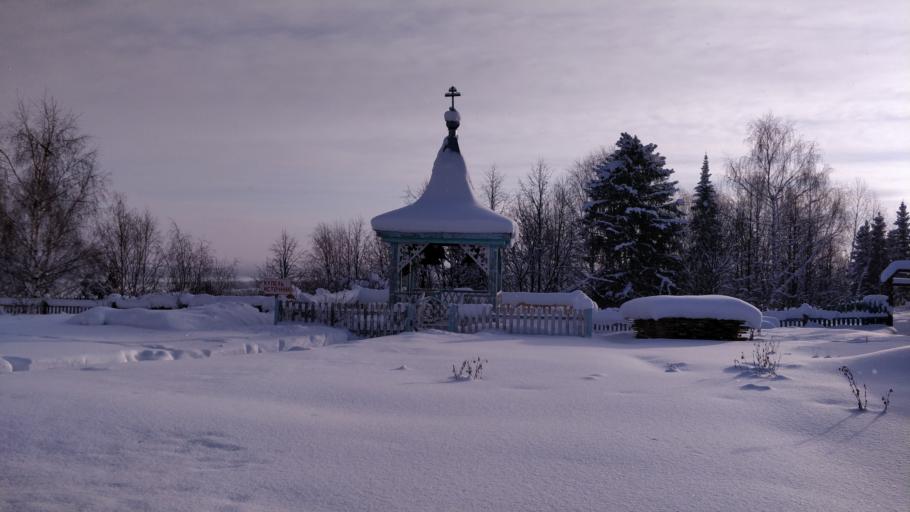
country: RU
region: Perm
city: Verkhnechusovskiye Gorodki
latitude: 58.2125
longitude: 57.0694
